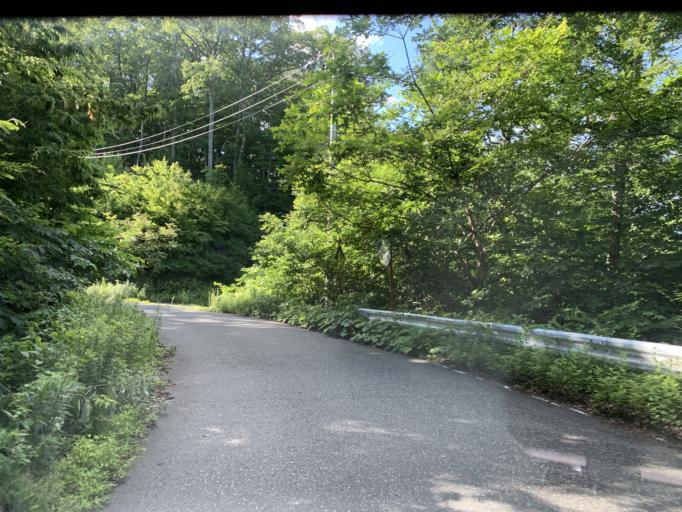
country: JP
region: Iwate
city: Ichinoseki
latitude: 38.9044
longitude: 140.8558
